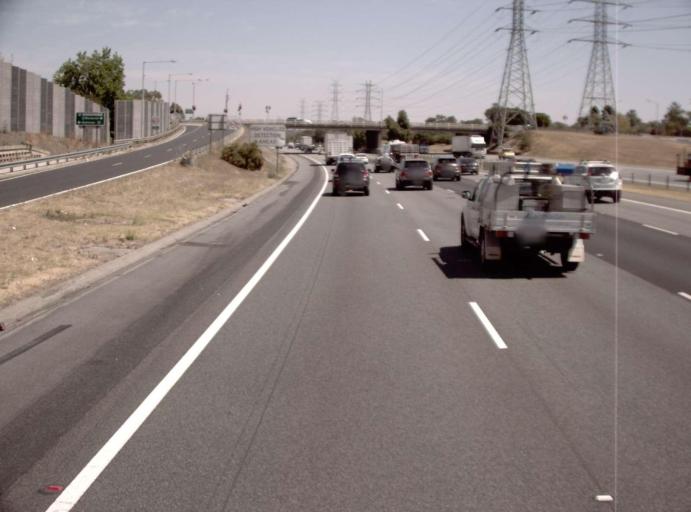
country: AU
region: Victoria
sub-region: Monash
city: Chadstone
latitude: -37.8873
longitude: 145.1105
